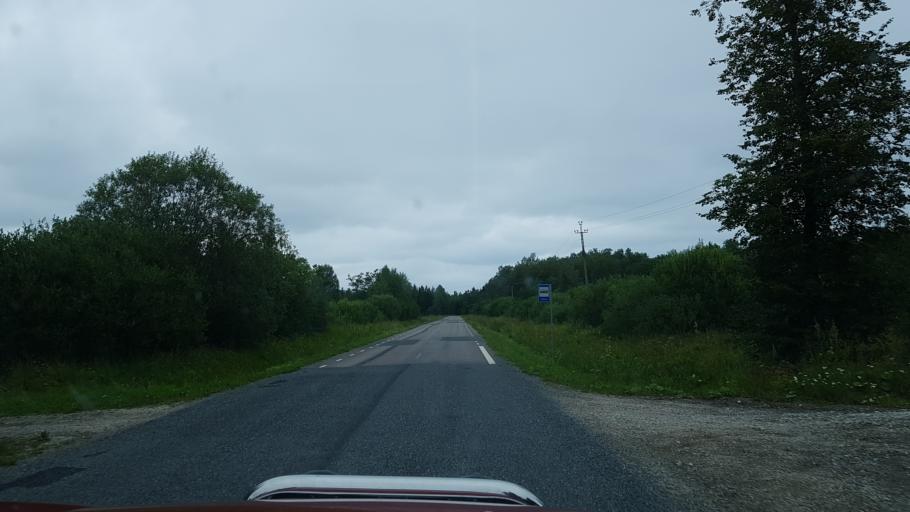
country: EE
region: Ida-Virumaa
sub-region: Johvi vald
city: Johvi
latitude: 59.4103
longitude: 27.4127
